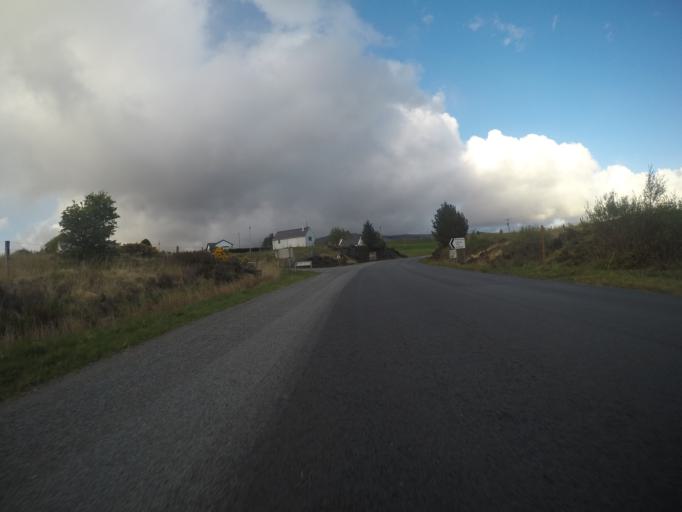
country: GB
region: Scotland
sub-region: Highland
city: Isle of Skye
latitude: 57.4534
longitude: -6.2984
